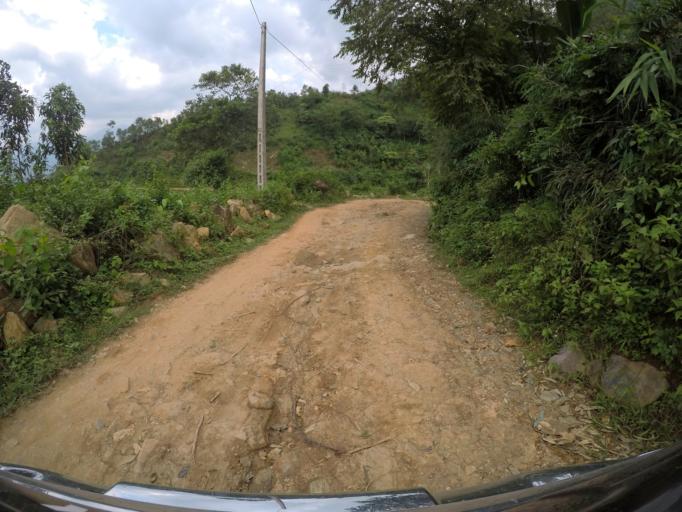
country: VN
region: Yen Bai
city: Son Thinh
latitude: 21.6811
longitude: 104.5765
